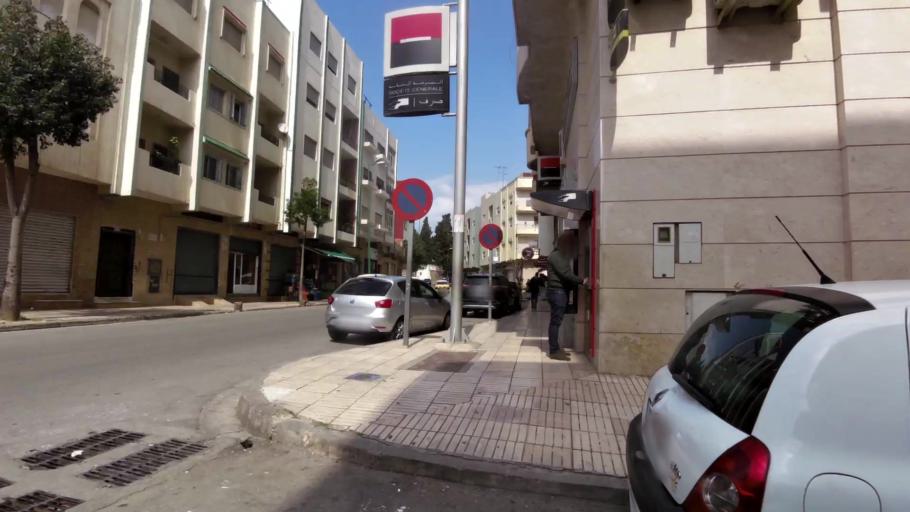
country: MA
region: Tanger-Tetouan
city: Tetouan
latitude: 35.5819
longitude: -5.3554
